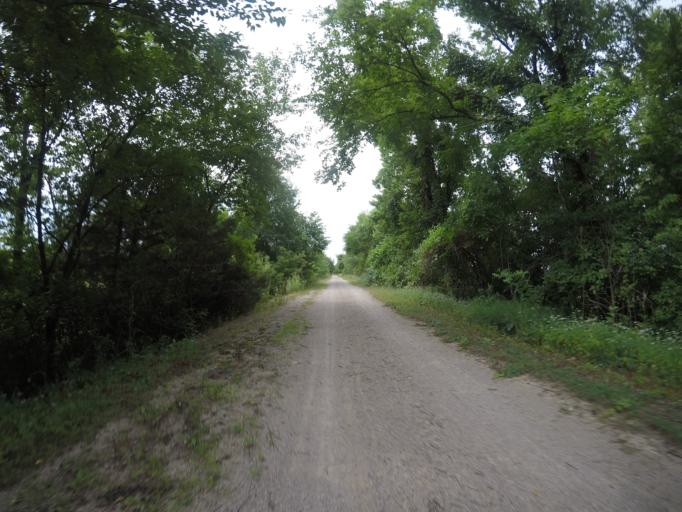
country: US
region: Kansas
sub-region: Franklin County
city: Ottawa
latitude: 38.4994
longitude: -95.2735
